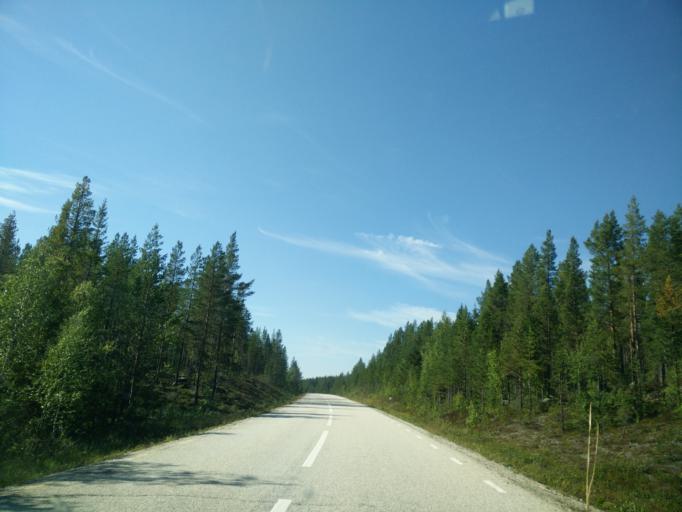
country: SE
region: Jaemtland
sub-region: Are Kommun
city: Jarpen
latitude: 62.8239
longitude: 13.4968
